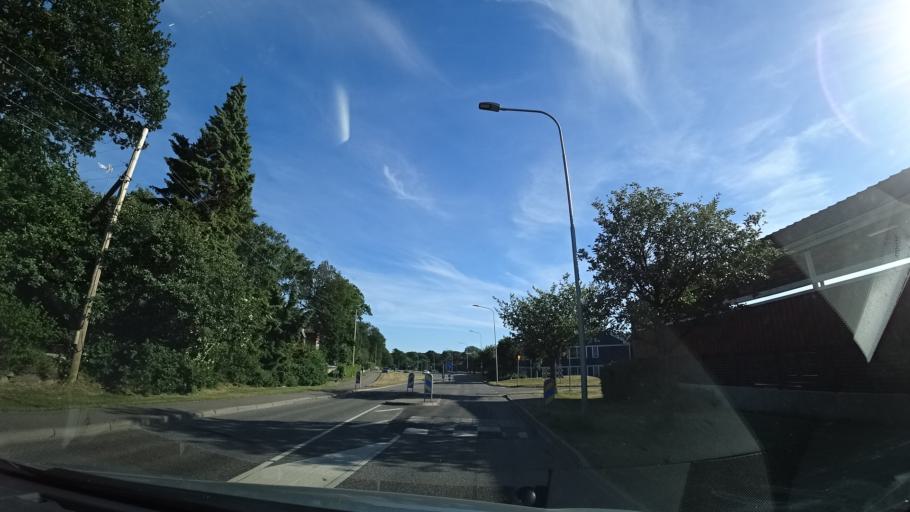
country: SE
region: Vaestra Goetaland
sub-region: Goteborg
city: Billdal
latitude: 57.5883
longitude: 11.9393
